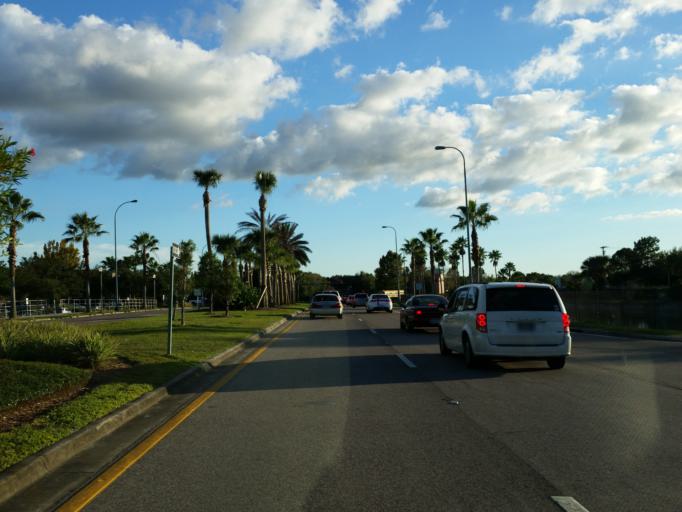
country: US
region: Florida
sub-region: Hillsborough County
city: Brandon
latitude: 27.9251
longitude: -82.3025
